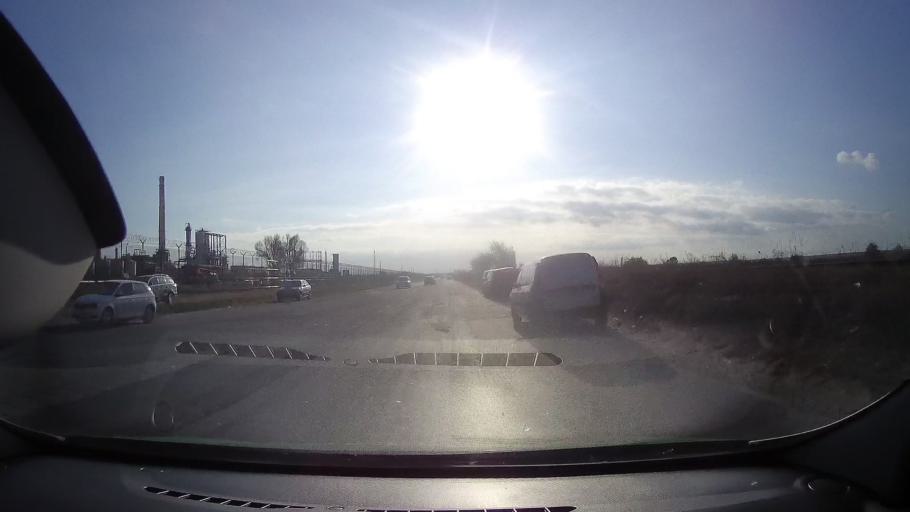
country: RO
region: Constanta
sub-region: Comuna Corbu
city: Corbu
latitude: 44.3438
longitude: 28.6414
